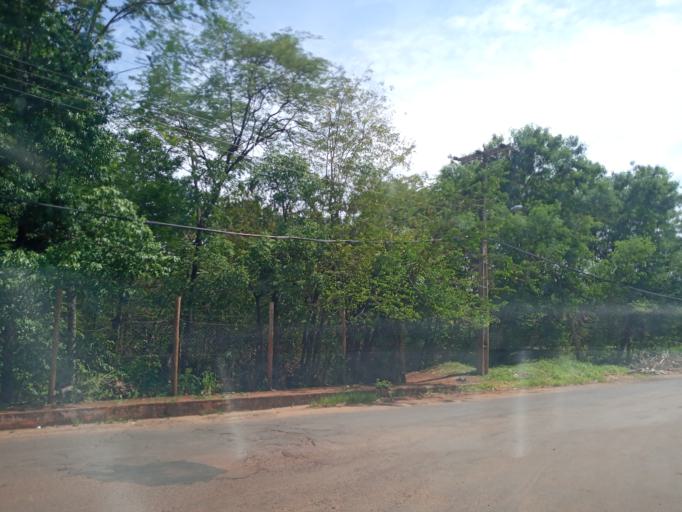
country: BR
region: Minas Gerais
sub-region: Ituiutaba
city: Ituiutaba
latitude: -18.9938
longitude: -49.4746
